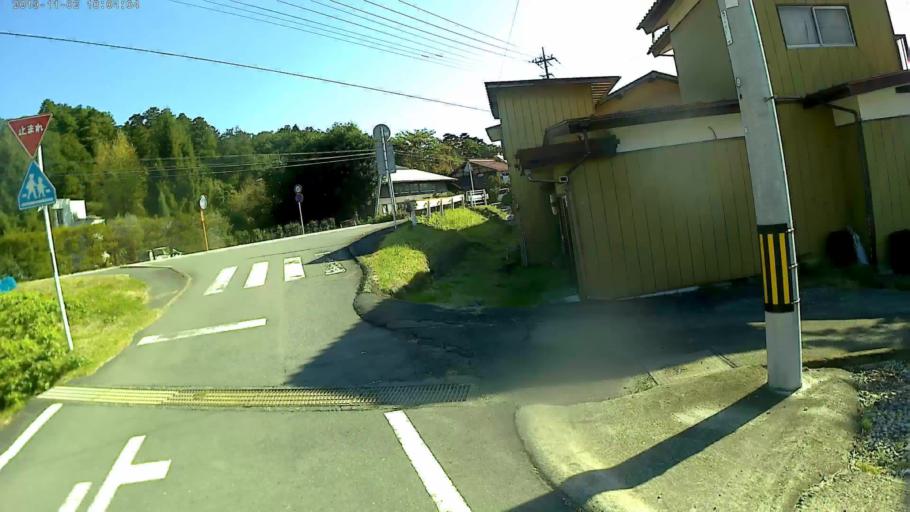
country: JP
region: Gunma
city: Annaka
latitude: 36.3191
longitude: 138.7859
